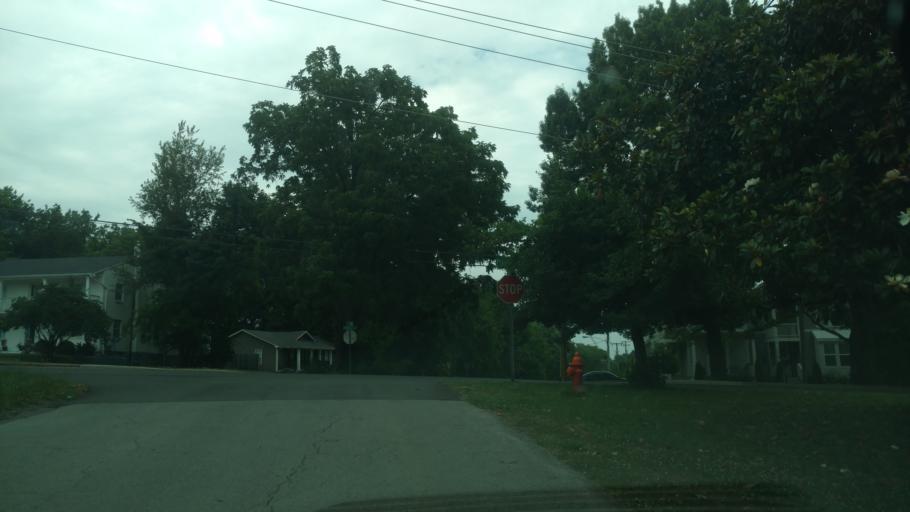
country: US
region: Tennessee
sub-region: Davidson County
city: Nashville
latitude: 36.1957
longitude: -86.7205
